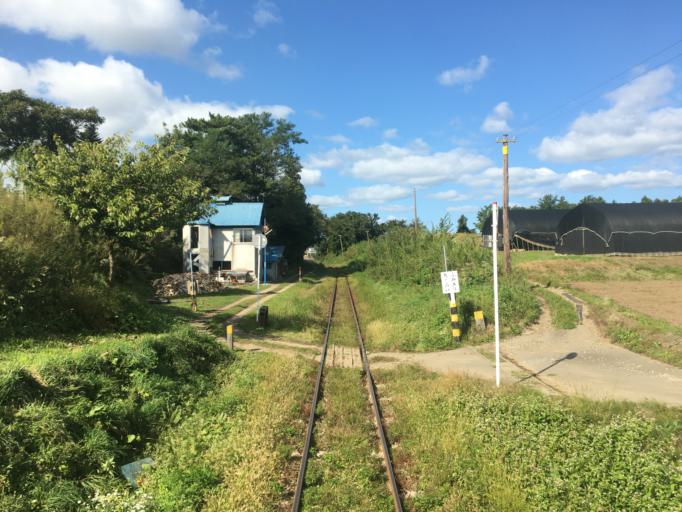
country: JP
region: Aomori
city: Goshogawara
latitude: 40.9578
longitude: 140.4436
